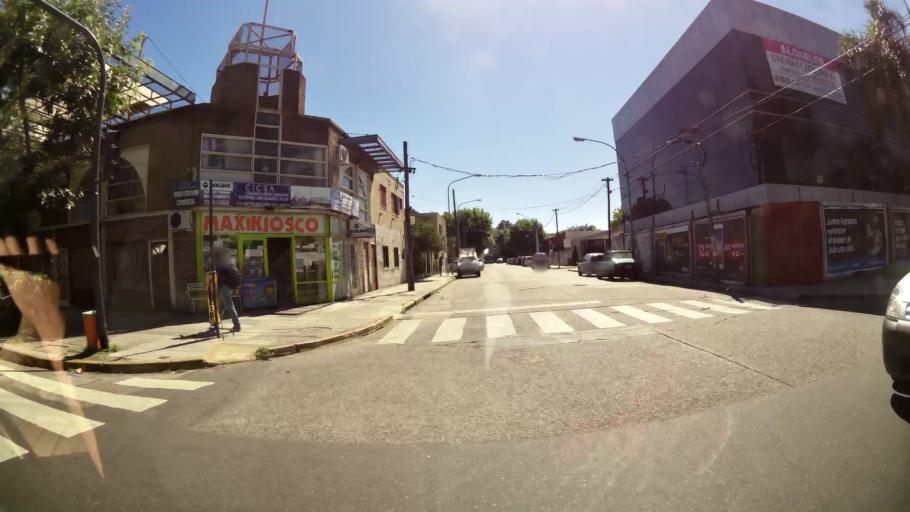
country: AR
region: Buenos Aires
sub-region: Partido de Vicente Lopez
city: Olivos
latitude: -34.5250
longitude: -58.5198
